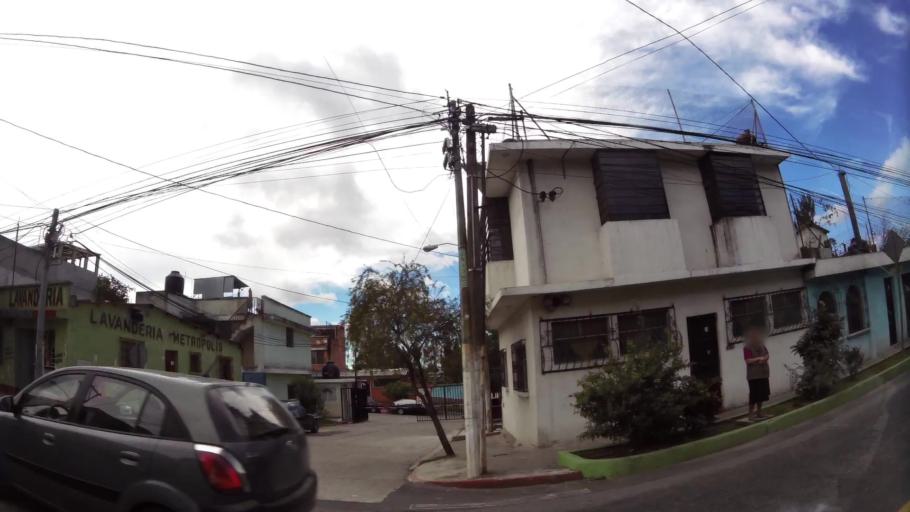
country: GT
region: Guatemala
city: Guatemala City
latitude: 14.5972
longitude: -90.5376
